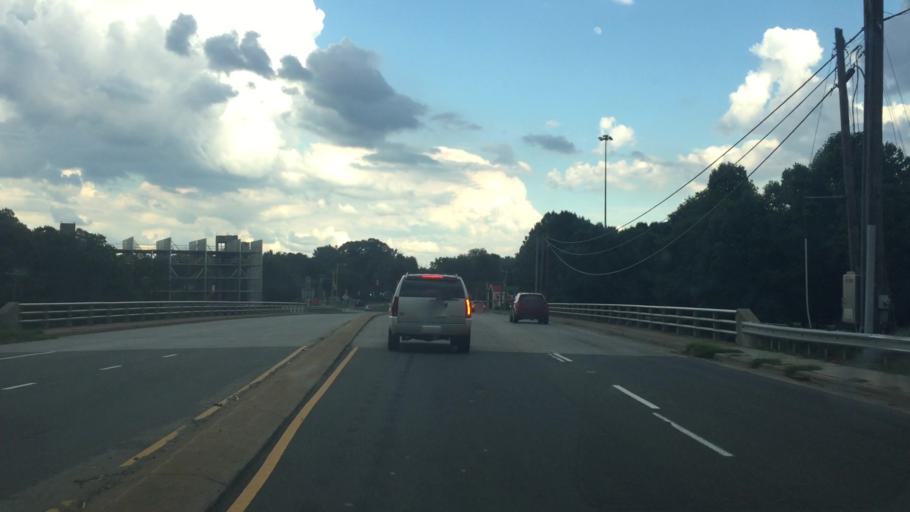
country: US
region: North Carolina
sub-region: Rowan County
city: Salisbury
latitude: 35.6427
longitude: -80.4812
